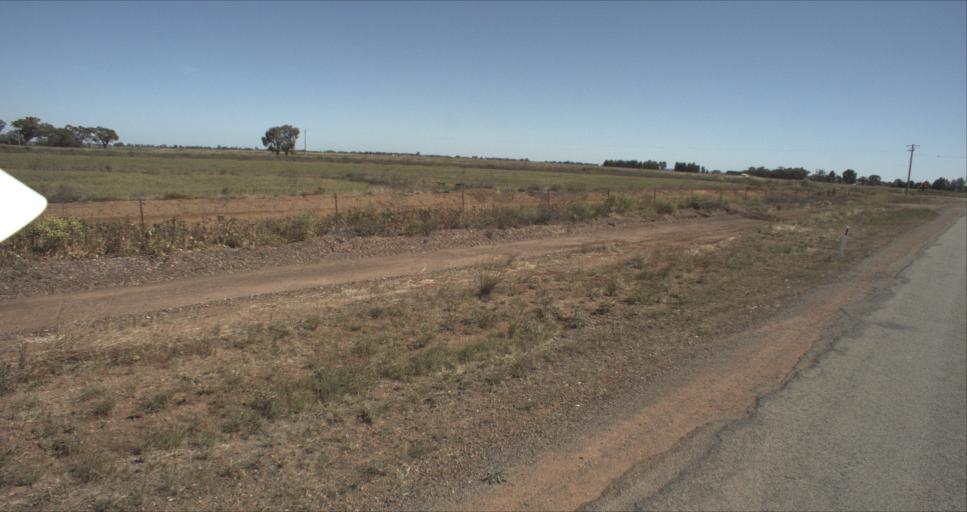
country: AU
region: New South Wales
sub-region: Leeton
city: Leeton
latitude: -34.5516
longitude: 146.3145
